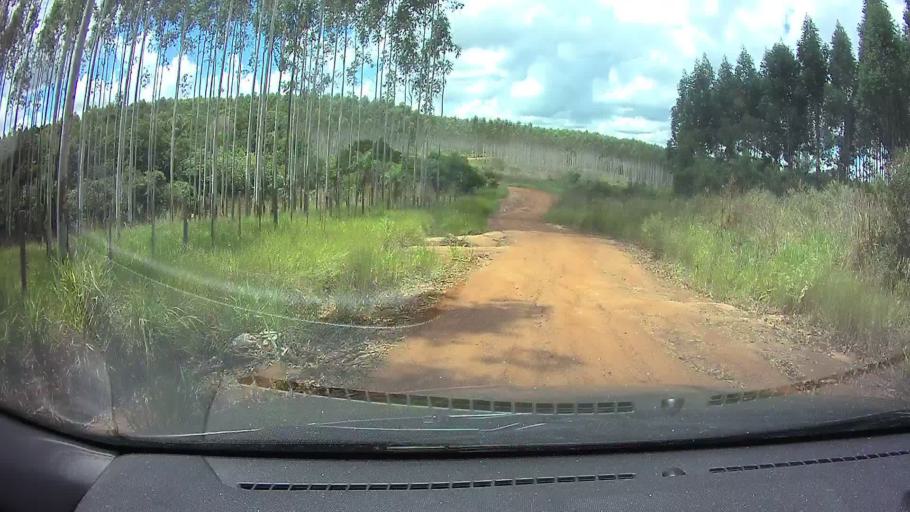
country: PY
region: Paraguari
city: La Colmena
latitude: -25.9660
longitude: -56.7486
